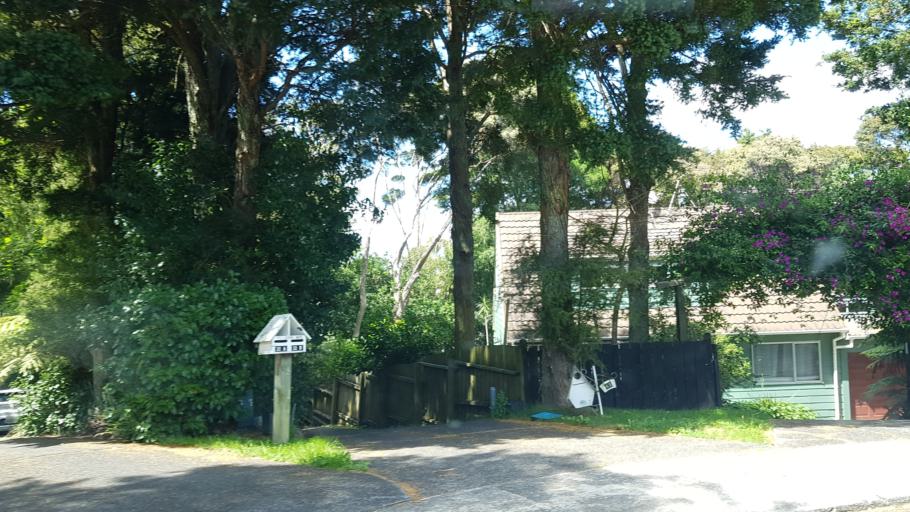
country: NZ
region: Auckland
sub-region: Auckland
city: North Shore
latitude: -36.7938
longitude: 174.7147
